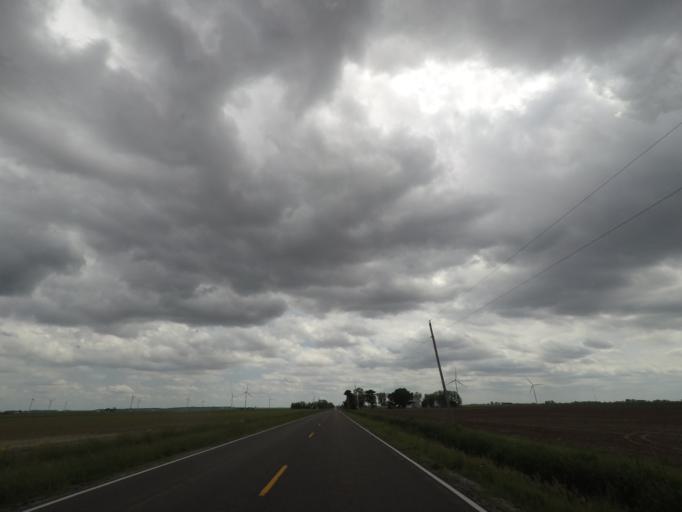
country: US
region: Illinois
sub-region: Macon County
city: Warrensburg
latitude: 39.9838
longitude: -89.0857
